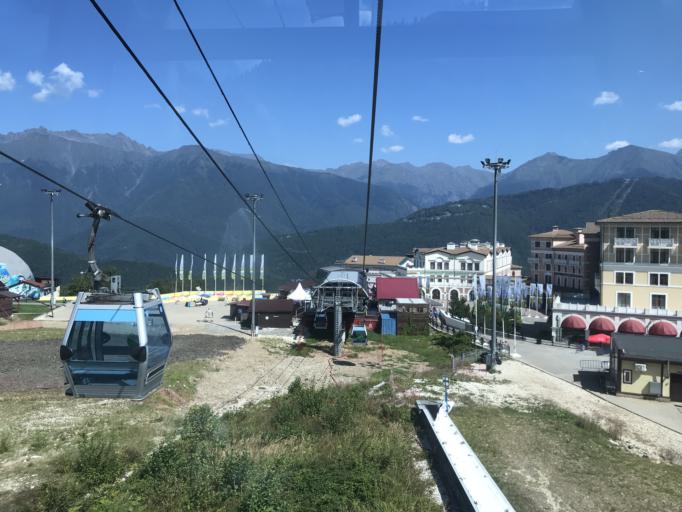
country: RU
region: Krasnodarskiy
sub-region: Sochi City
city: Krasnaya Polyana
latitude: 43.6679
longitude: 40.2583
